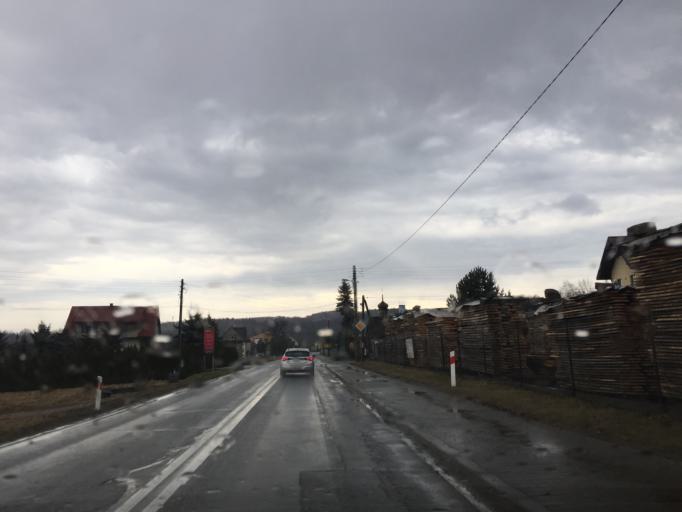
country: PL
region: Lesser Poland Voivodeship
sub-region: Powiat wadowicki
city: Izdebnik
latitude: 49.8694
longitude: 19.7932
